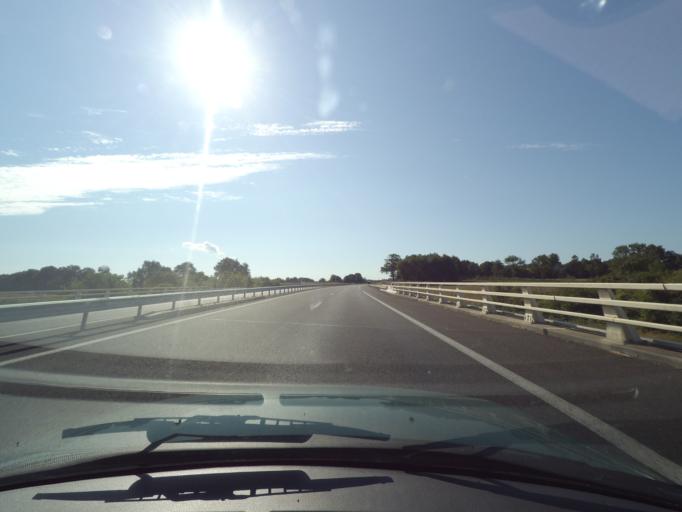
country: FR
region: Poitou-Charentes
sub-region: Departement de la Vienne
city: Terce
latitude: 46.4840
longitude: 0.5313
